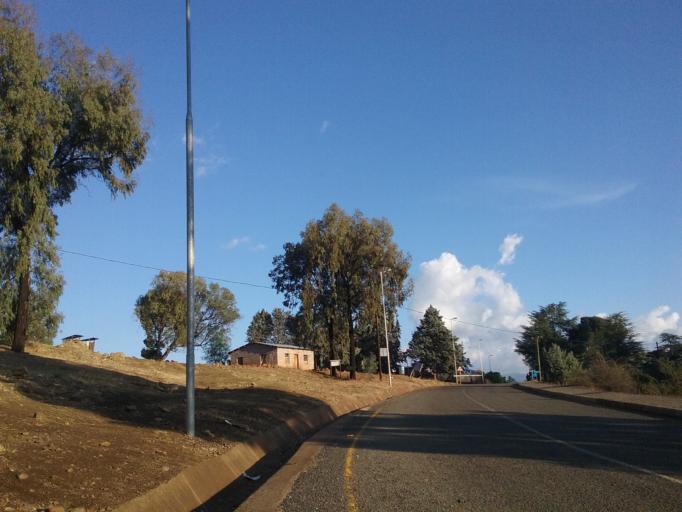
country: LS
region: Quthing
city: Quthing
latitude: -30.4099
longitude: 27.7080
